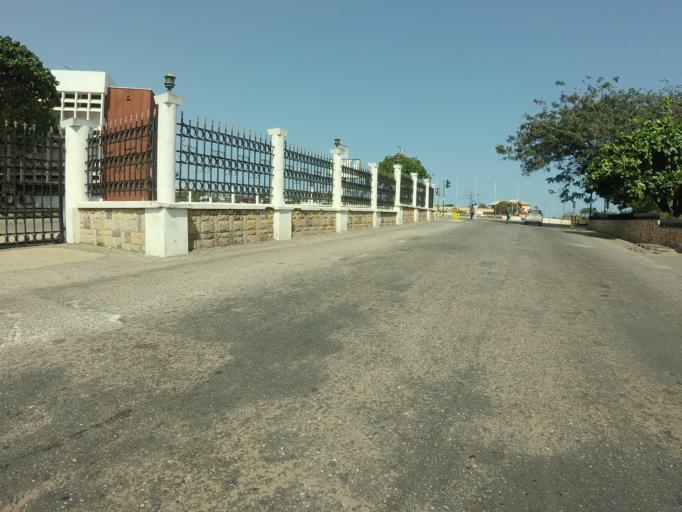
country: GH
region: Greater Accra
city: Accra
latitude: 5.5440
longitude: -0.2051
